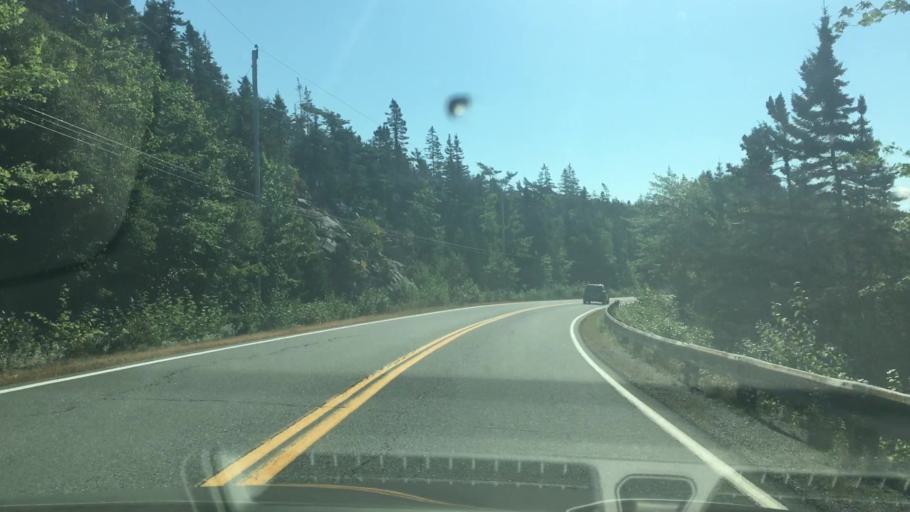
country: CA
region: Nova Scotia
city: Cole Harbour
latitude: 44.8118
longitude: -62.8374
